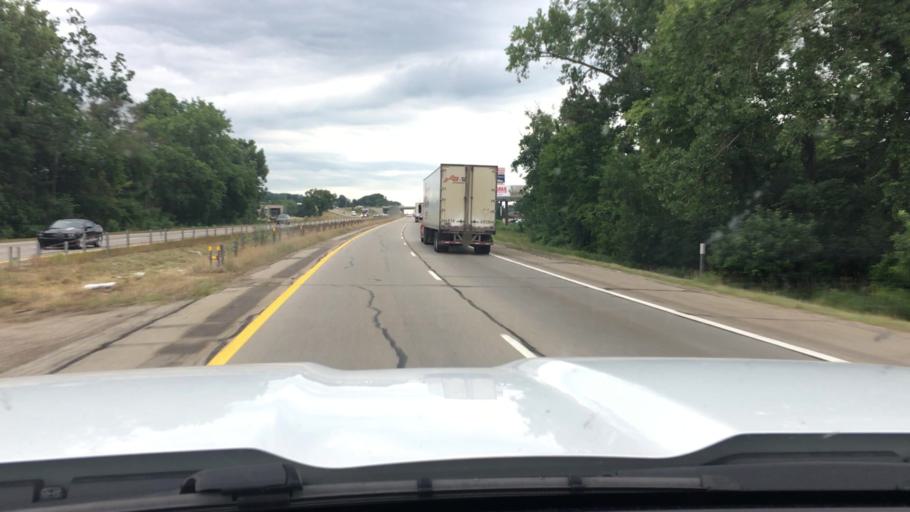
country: US
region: Michigan
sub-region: Kent County
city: Cutlerville
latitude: 42.8186
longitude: -85.6690
